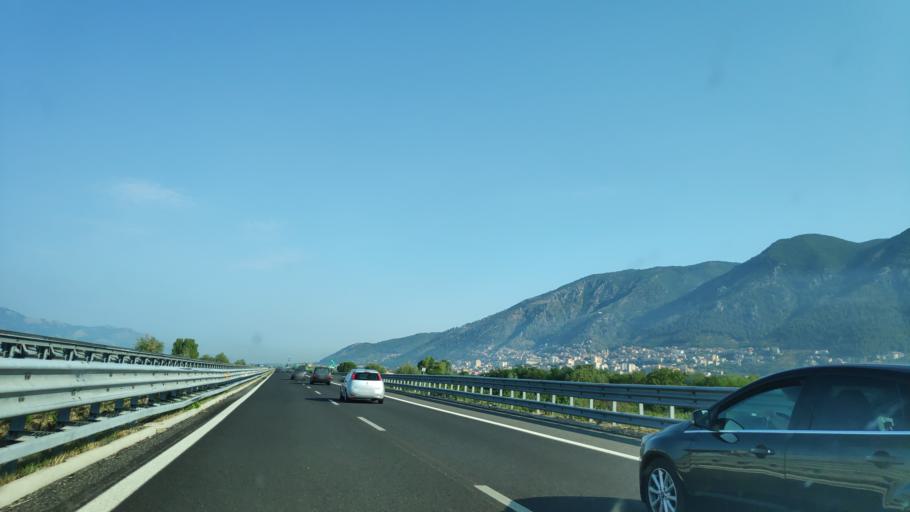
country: IT
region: Campania
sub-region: Provincia di Salerno
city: Sala Consilina
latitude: 40.3760
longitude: 15.5980
